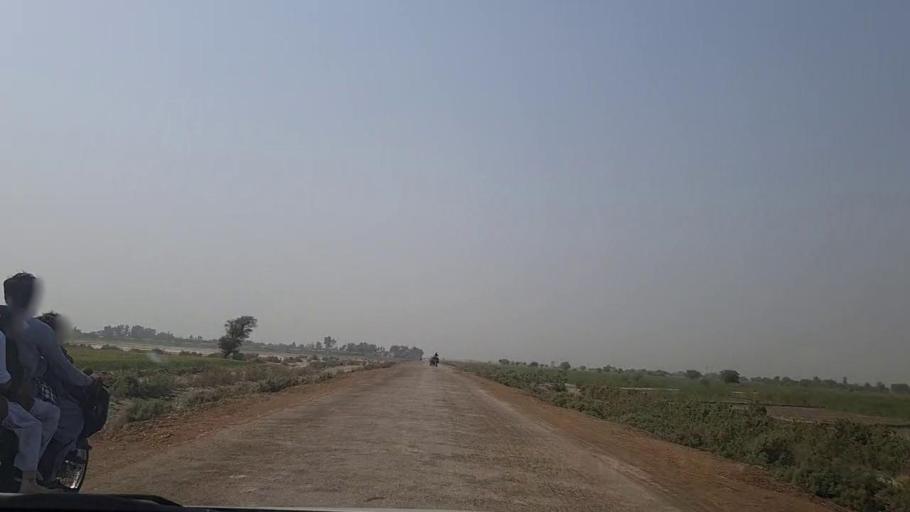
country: PK
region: Sindh
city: Pithoro
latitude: 25.5465
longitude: 69.2377
